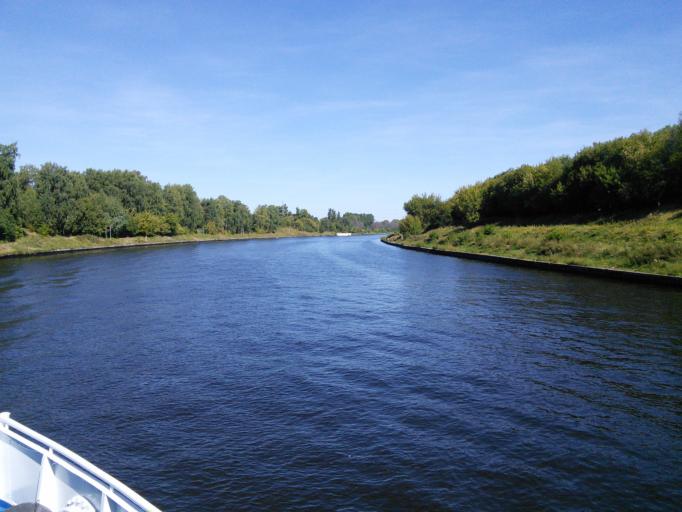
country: RU
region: Moskovskaya
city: Dolgoprudnyy
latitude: 55.9438
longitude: 37.4795
